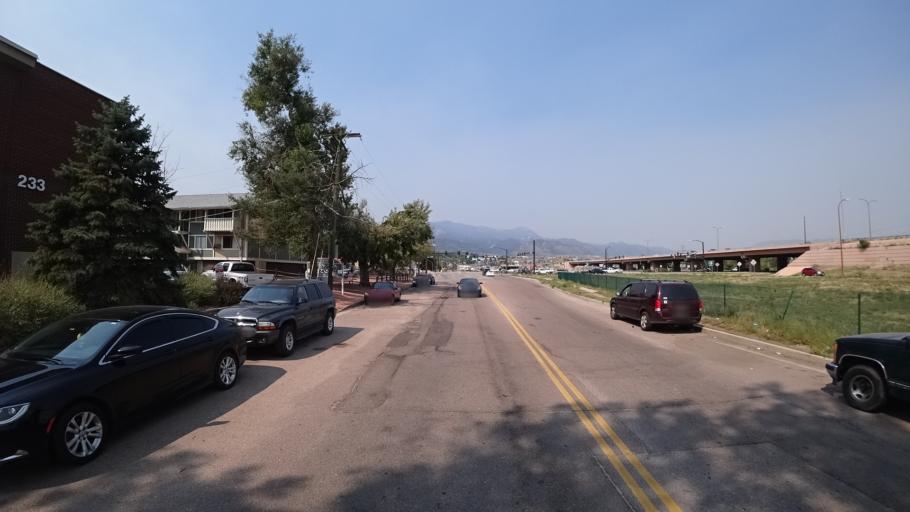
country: US
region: Colorado
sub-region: El Paso County
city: Colorado Springs
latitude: 38.8140
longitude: -104.8209
